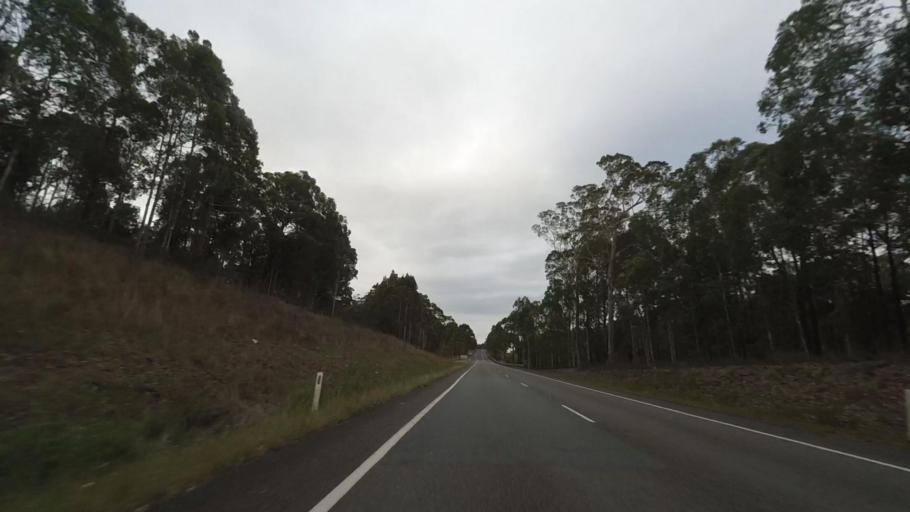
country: AU
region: New South Wales
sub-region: Shoalhaven Shire
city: Milton
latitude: -35.1297
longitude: 150.4692
